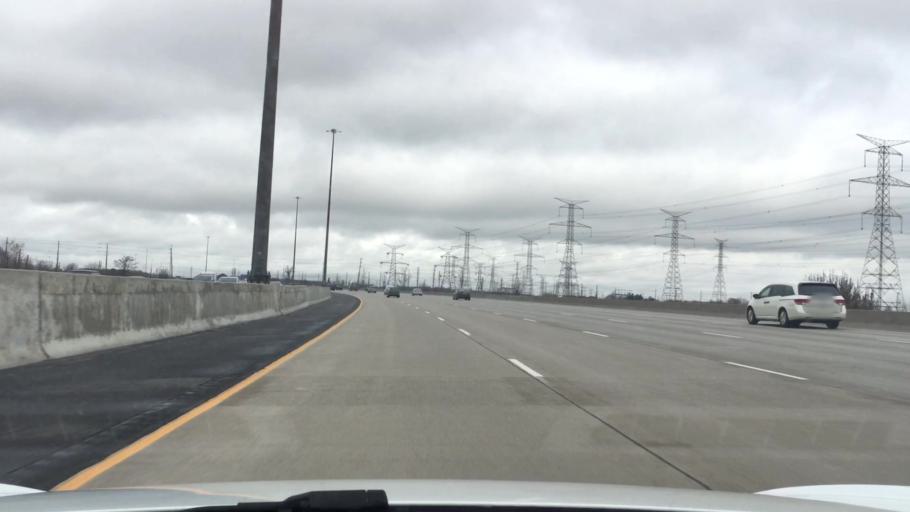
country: CA
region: Ontario
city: Concord
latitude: 43.8021
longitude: -79.4819
